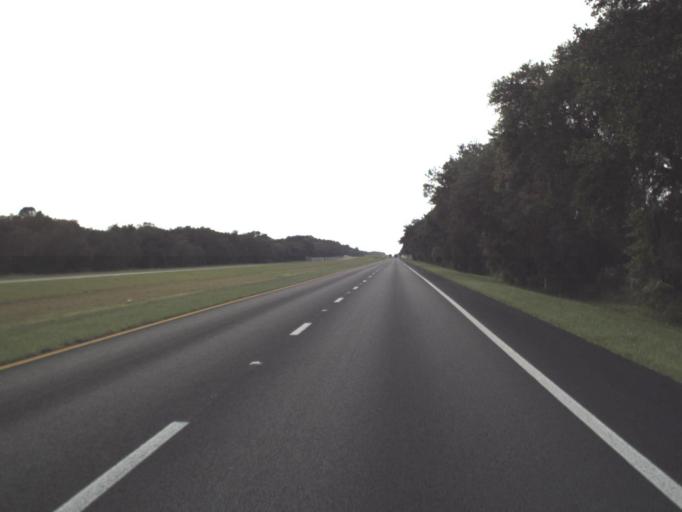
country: US
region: Florida
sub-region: Hendry County
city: Port LaBelle
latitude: 26.7685
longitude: -81.3169
